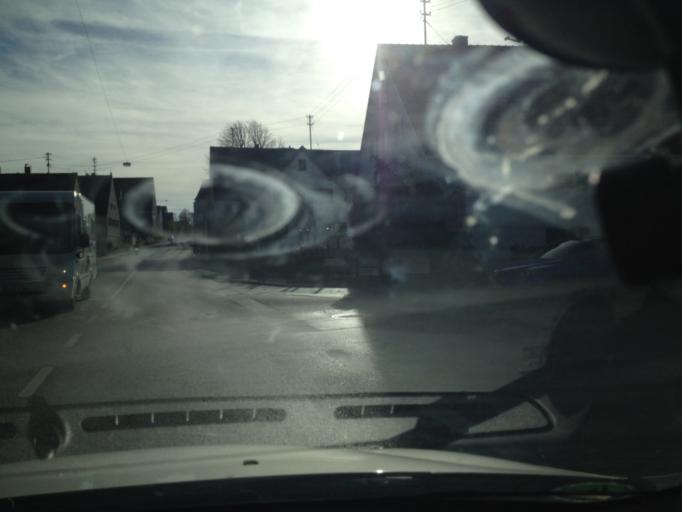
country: DE
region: Bavaria
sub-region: Swabia
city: Bobingen
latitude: 48.2784
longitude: 10.8405
